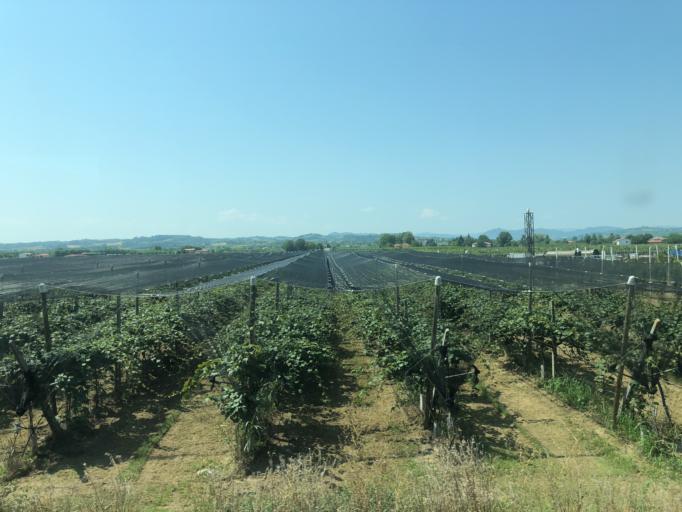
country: IT
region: Emilia-Romagna
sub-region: Provincia di Ravenna
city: Castel Bolognese
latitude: 44.3184
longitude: 11.8213
